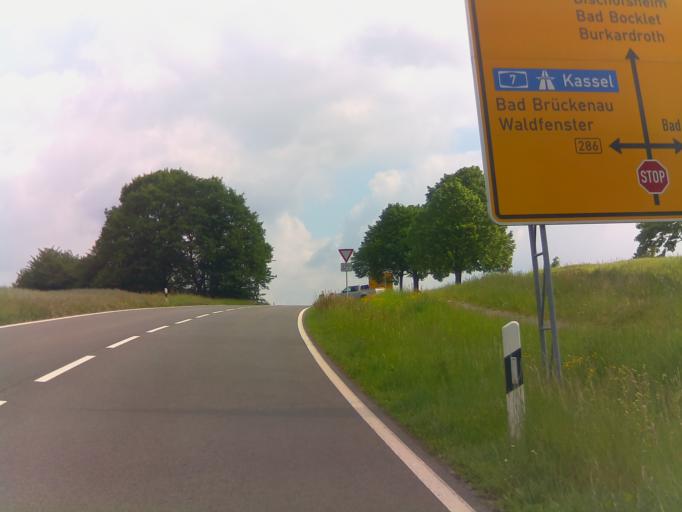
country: DE
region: Bavaria
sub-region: Regierungsbezirk Unterfranken
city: Burkardroth
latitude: 50.2485
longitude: 9.9789
